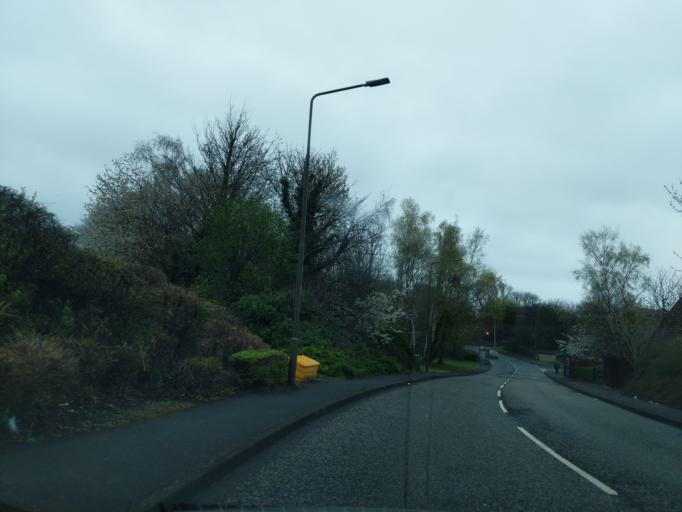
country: GB
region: Scotland
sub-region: East Lothian
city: Musselburgh
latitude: 55.9392
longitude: -3.0734
